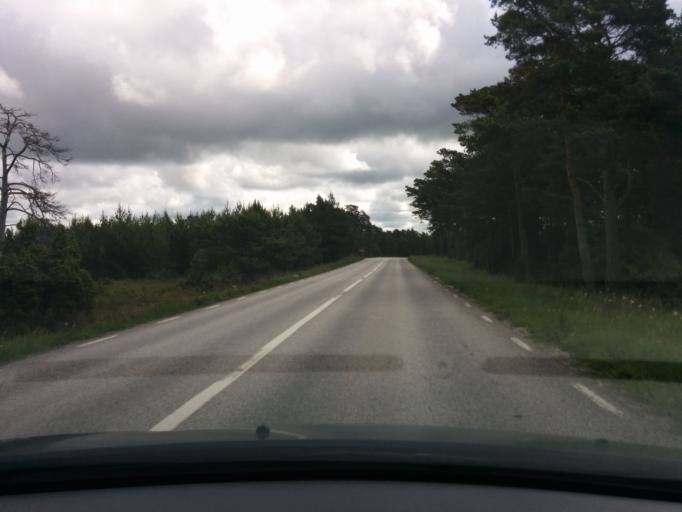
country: SE
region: Gotland
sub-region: Gotland
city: Visby
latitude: 57.6381
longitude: 18.3931
